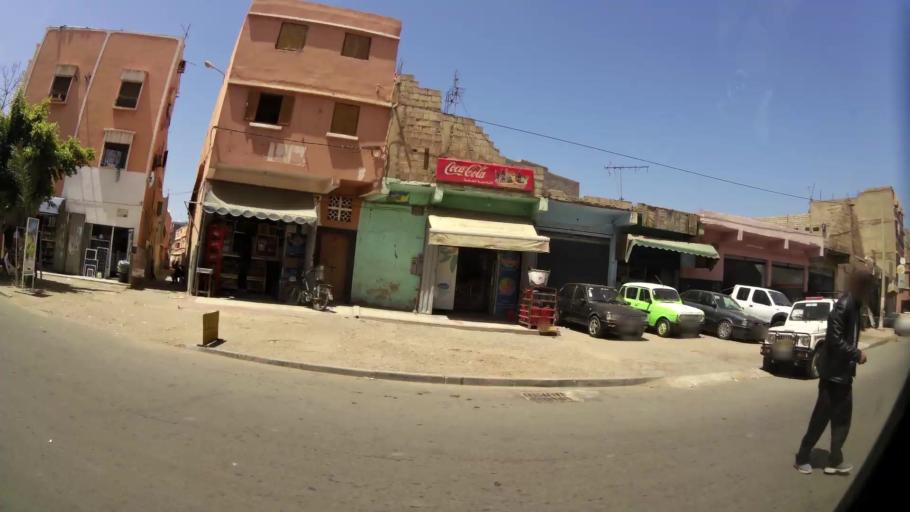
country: MA
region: Souss-Massa-Draa
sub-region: Inezgane-Ait Mellou
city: Inezgane
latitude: 30.3451
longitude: -9.4973
